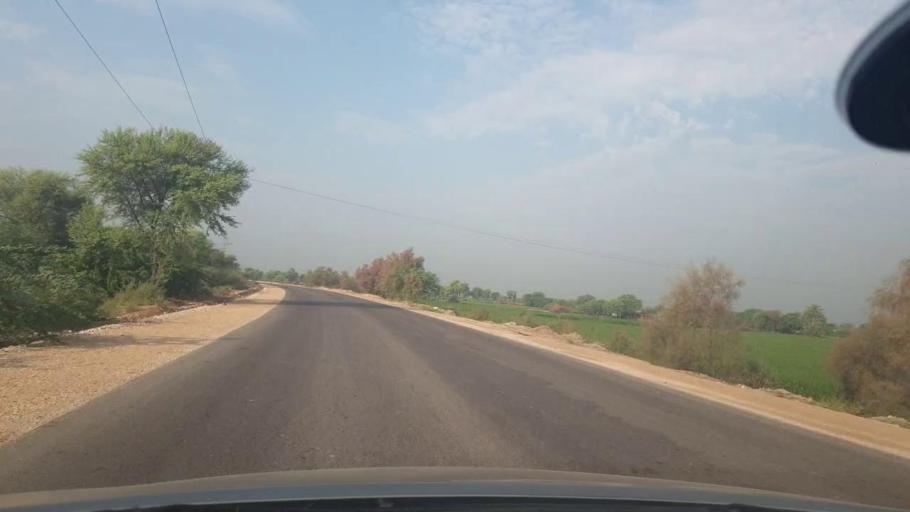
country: PK
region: Sindh
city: Jacobabad
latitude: 28.2446
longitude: 68.3966
